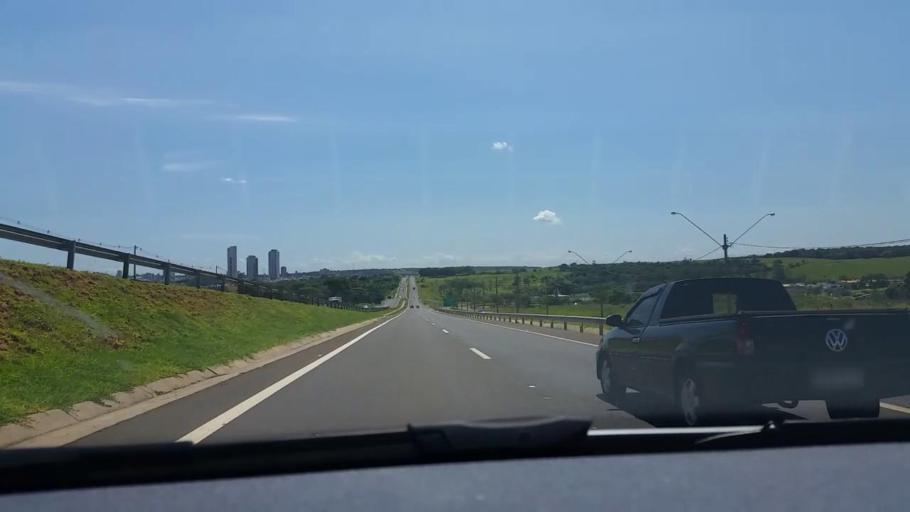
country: BR
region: Sao Paulo
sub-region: Bauru
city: Bauru
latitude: -22.3899
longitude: -49.0768
